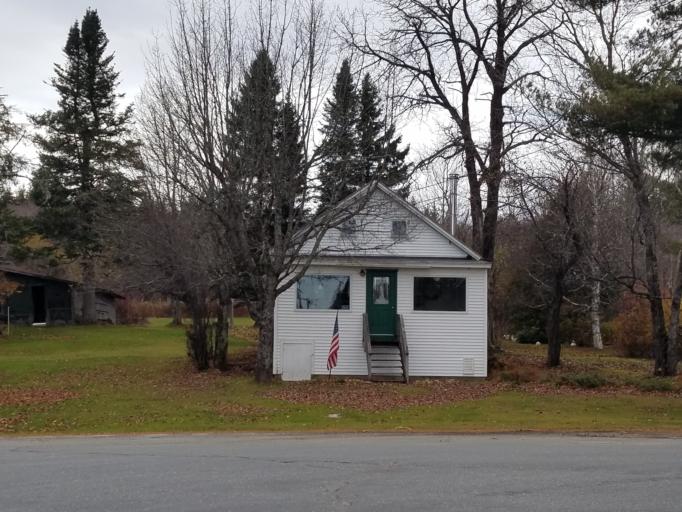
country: US
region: Maine
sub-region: Penobscot County
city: Patten
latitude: 46.2061
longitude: -68.3307
